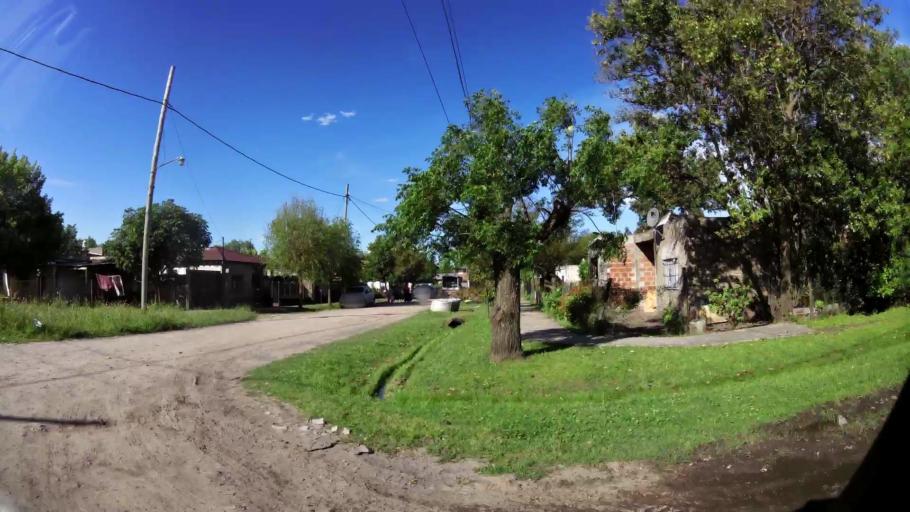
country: AR
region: Buenos Aires
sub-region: Partido de Almirante Brown
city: Adrogue
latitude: -34.8267
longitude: -58.3499
